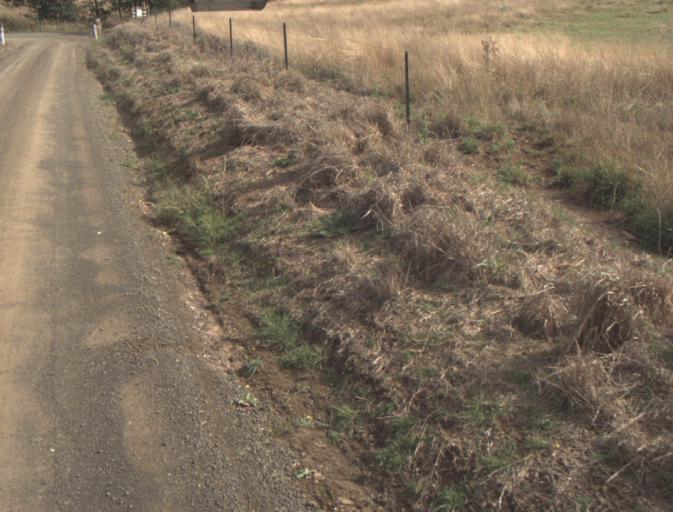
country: AU
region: Tasmania
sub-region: Launceston
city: Mayfield
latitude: -41.1912
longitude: 147.1894
